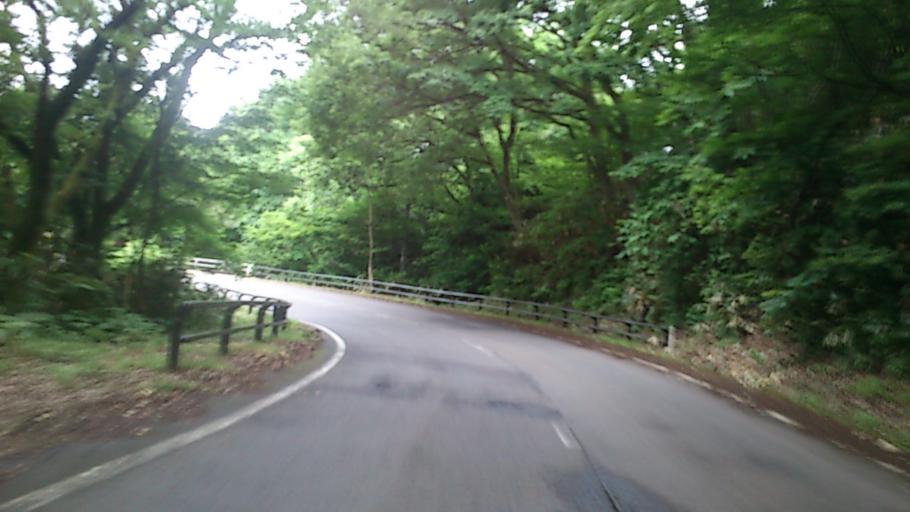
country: JP
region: Yamagata
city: Yuza
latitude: 39.1724
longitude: 139.9484
